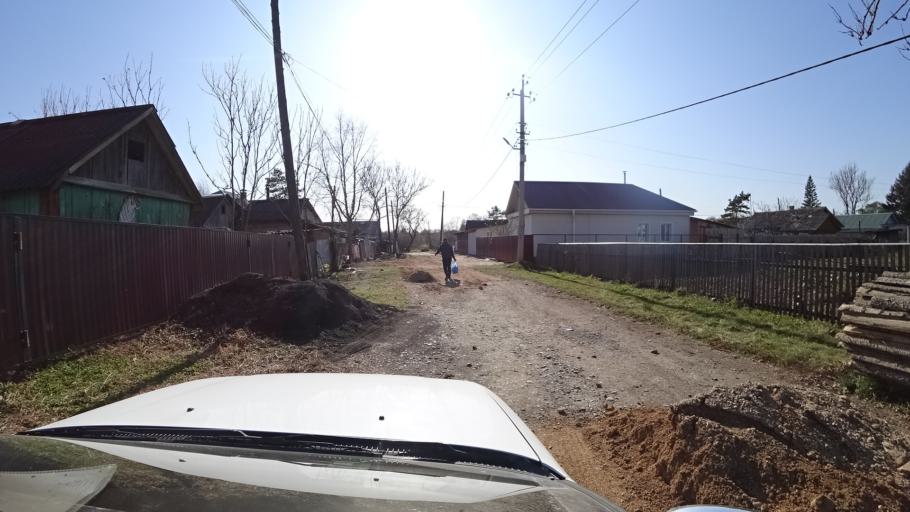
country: RU
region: Primorskiy
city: Dal'nerechensk
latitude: 45.9248
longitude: 133.7185
